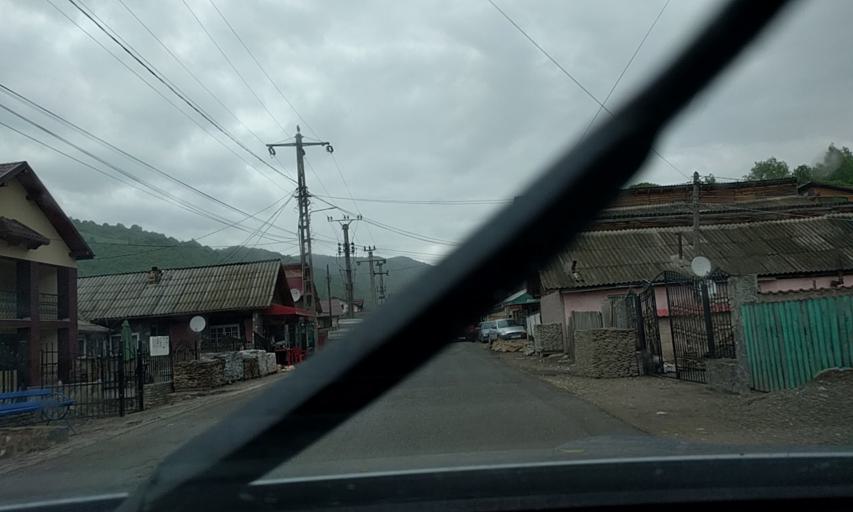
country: RO
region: Dambovita
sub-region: Comuna Moroeni
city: Glod
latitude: 45.2388
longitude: 25.4475
